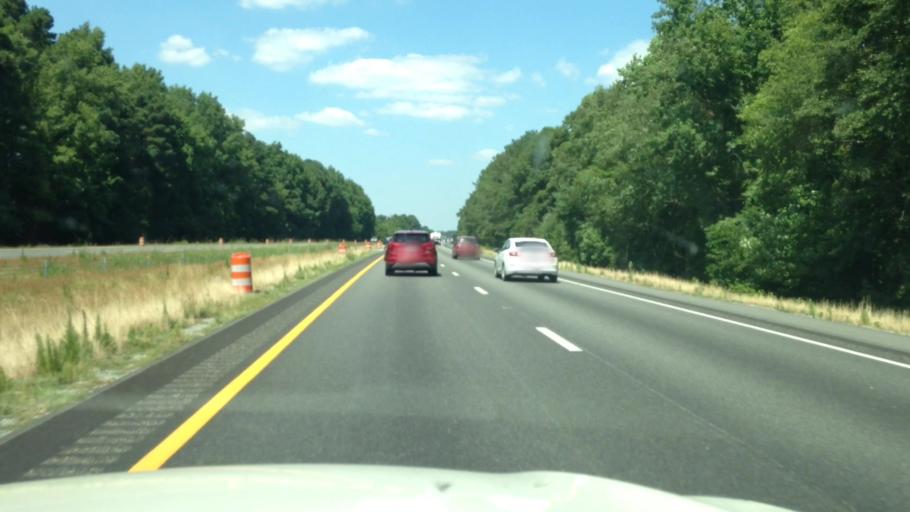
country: US
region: North Carolina
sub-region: Johnston County
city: Smithfield
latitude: 35.4730
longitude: -78.3739
